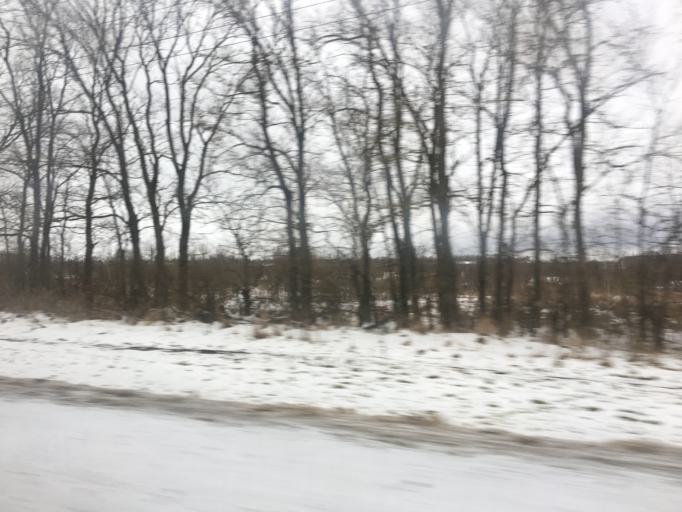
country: RU
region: Tula
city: Pervomayskiy
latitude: 54.0441
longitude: 37.5278
